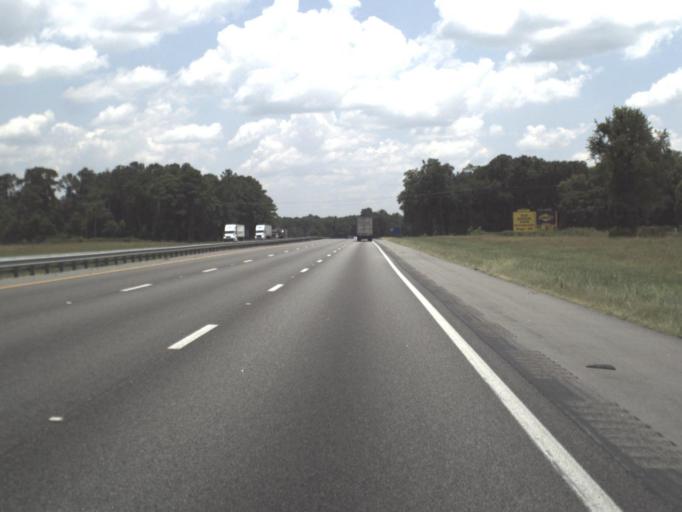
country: US
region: Florida
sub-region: Hamilton County
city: Jasper
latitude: 30.5291
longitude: -83.0683
